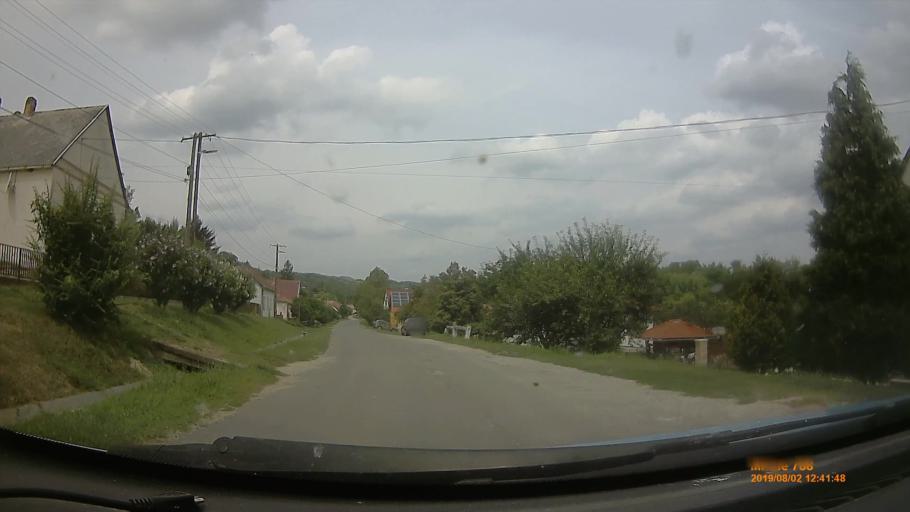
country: HU
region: Baranya
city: Buekkoesd
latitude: 46.0871
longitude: 17.9766
